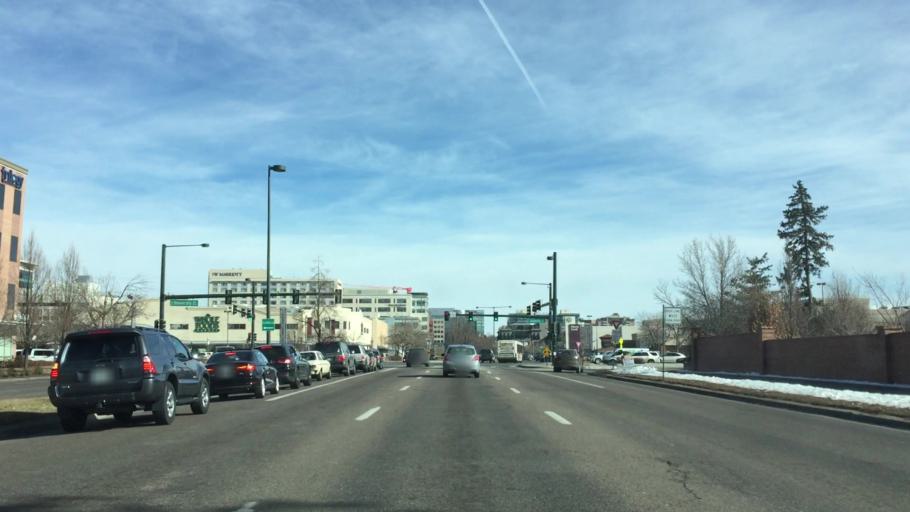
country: US
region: Colorado
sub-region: Arapahoe County
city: Glendale
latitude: 39.7182
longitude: -104.9604
